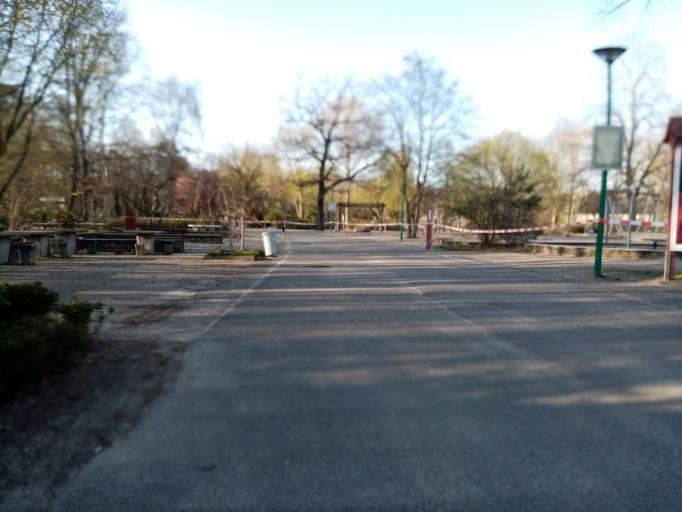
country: DE
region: Berlin
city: Oberschoneweide
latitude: 52.4623
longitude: 13.5473
